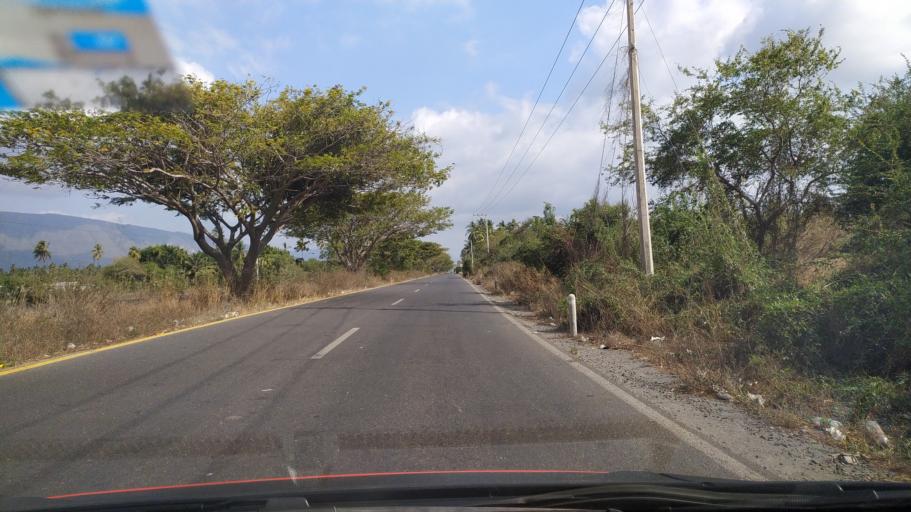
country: MX
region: Colima
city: Tecoman
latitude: 18.9432
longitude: -103.8824
